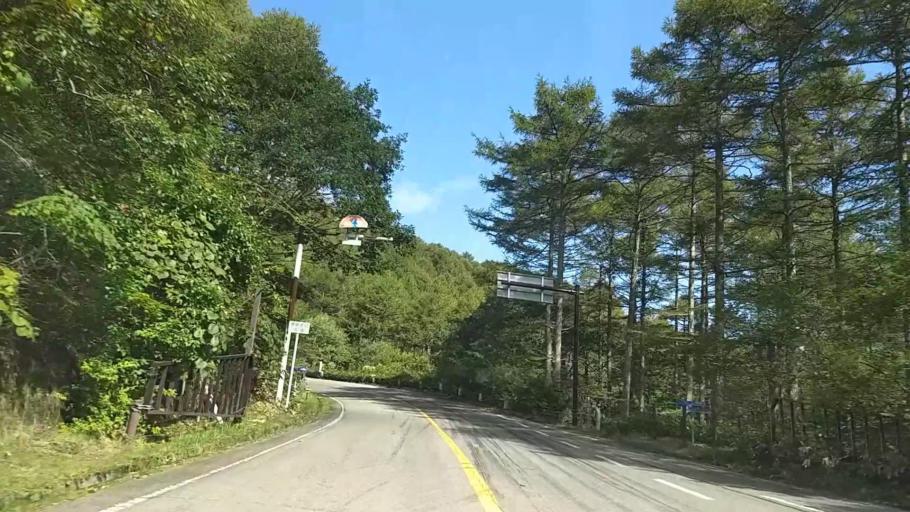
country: JP
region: Nagano
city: Suwa
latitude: 36.1486
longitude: 138.1424
